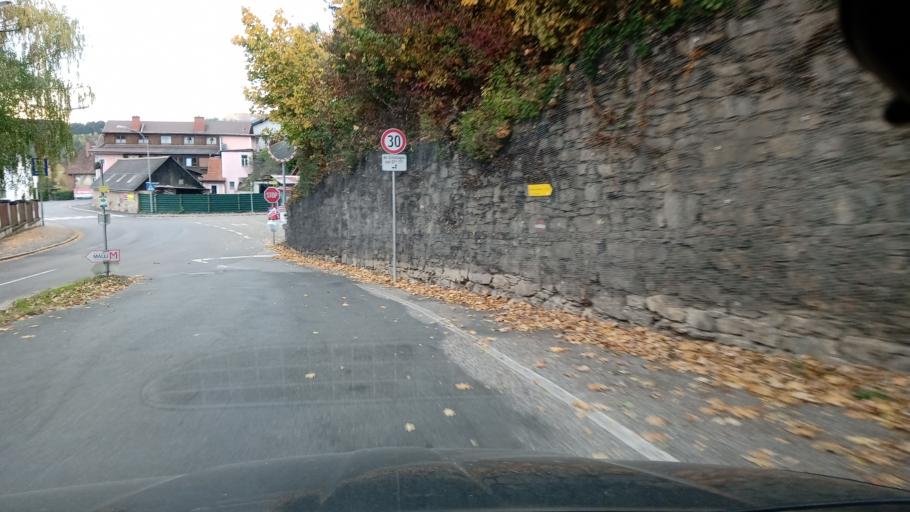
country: AT
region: Styria
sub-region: Politischer Bezirk Leoben
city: Leoben
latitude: 47.3896
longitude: 15.1022
